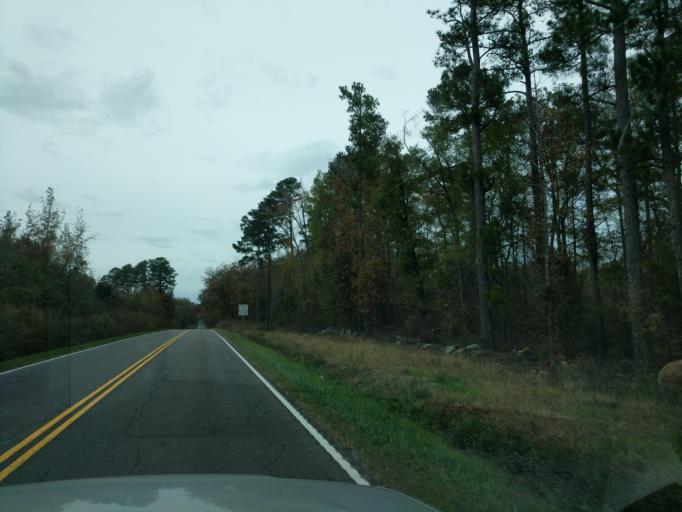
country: US
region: South Carolina
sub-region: Lexington County
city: Batesburg
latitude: 33.9369
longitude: -81.6077
